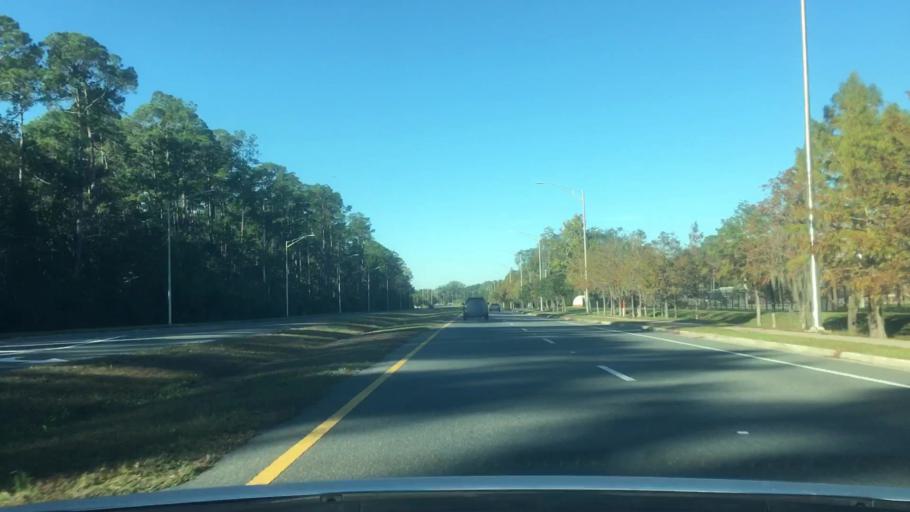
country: US
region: Florida
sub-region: Duval County
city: Jacksonville
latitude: 30.4761
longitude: -81.6163
